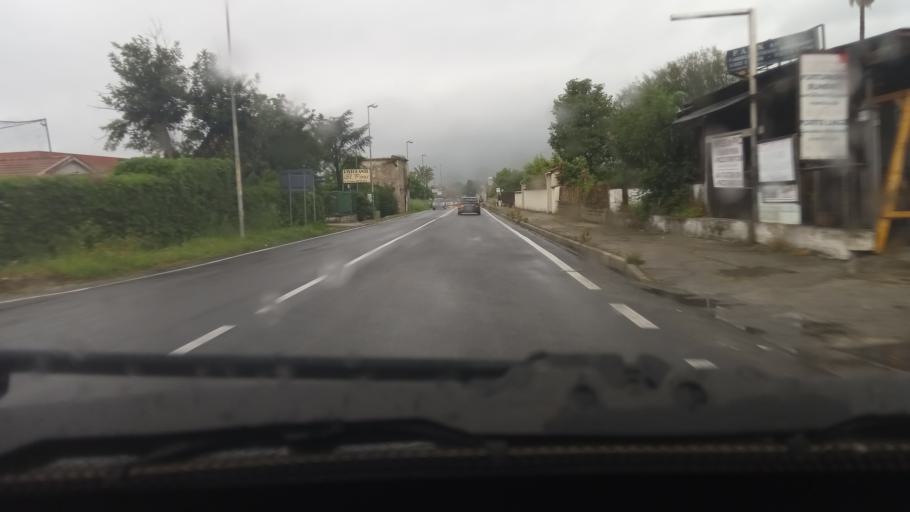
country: IT
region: Latium
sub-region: Provincia di Latina
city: Penitro
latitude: 41.2616
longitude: 13.6863
